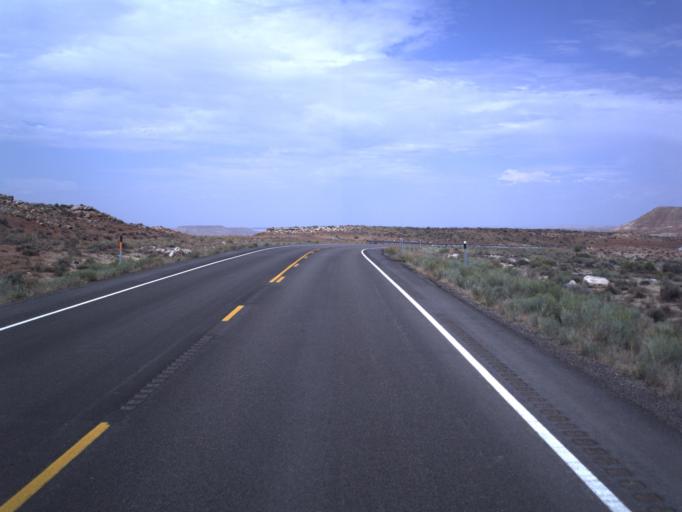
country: US
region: Utah
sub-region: Uintah County
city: Naples
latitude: 40.2625
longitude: -109.4476
